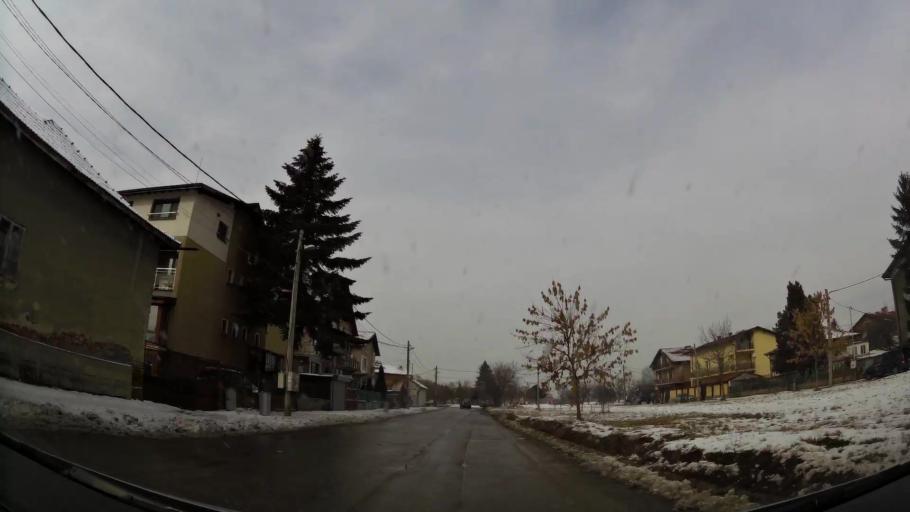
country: BG
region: Sofia-Capital
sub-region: Stolichna Obshtina
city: Sofia
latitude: 42.7128
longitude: 23.4052
